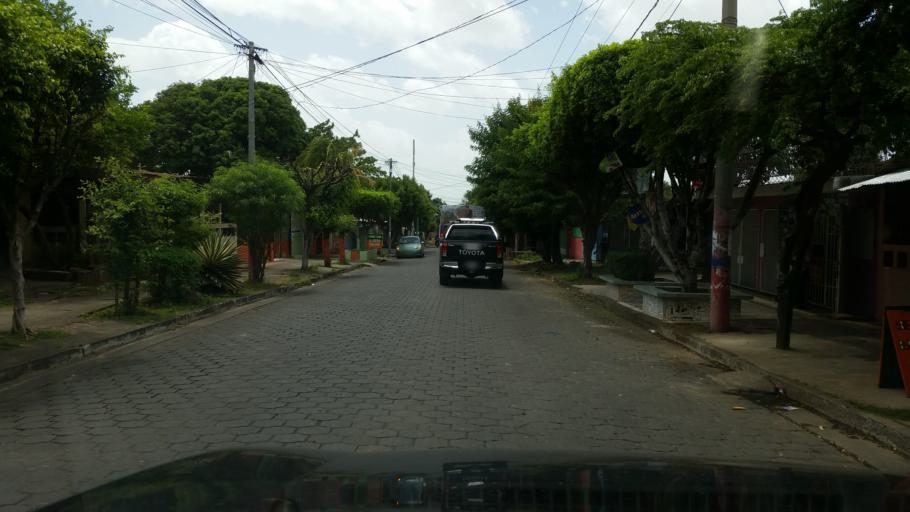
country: NI
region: Managua
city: Managua
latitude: 12.1436
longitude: -86.2097
